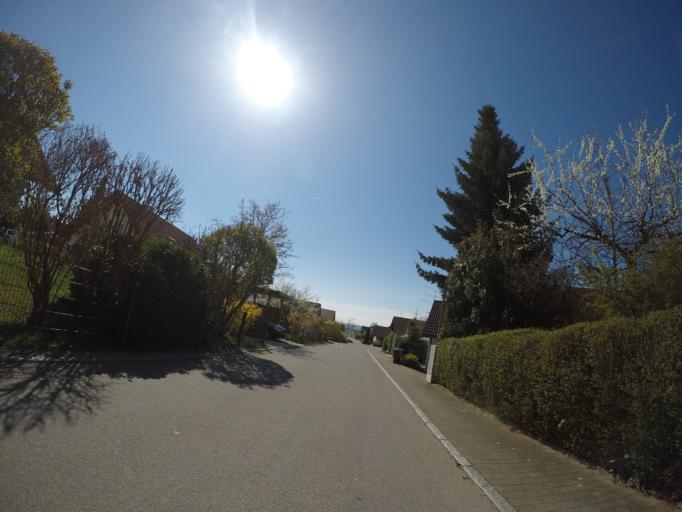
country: DE
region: Baden-Wuerttemberg
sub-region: Tuebingen Region
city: Wilhelmsdorf
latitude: 47.8633
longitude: 9.4294
